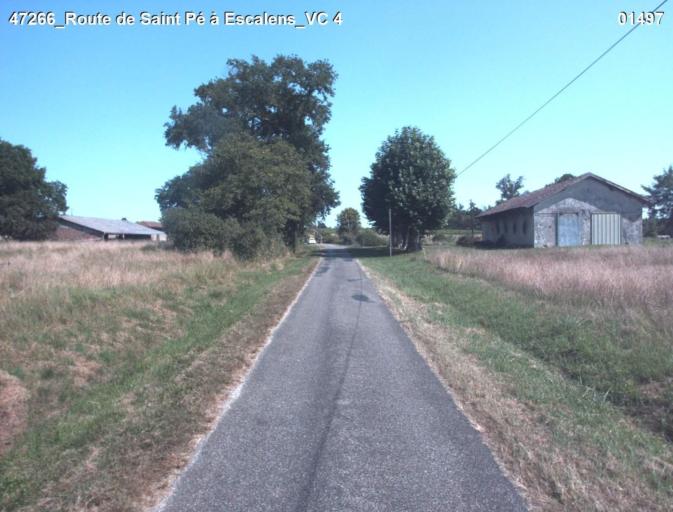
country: FR
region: Aquitaine
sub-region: Departement des Landes
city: Gabarret
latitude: 44.0003
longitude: 0.0783
